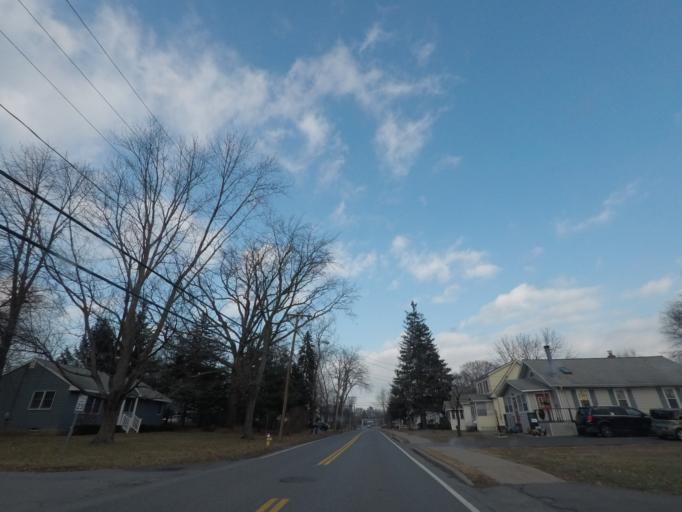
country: US
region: New York
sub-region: Albany County
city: Colonie
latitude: 42.7137
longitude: -73.8334
